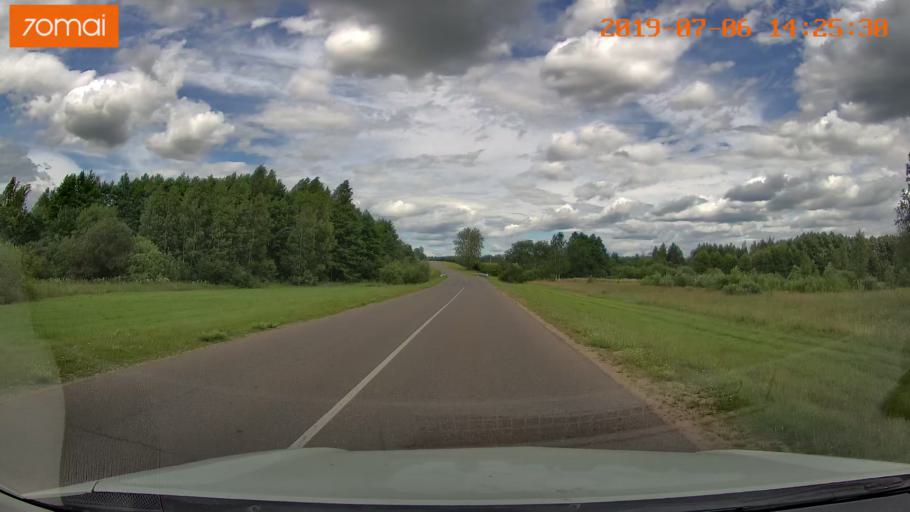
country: BY
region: Minsk
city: Ivyanyets
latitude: 53.9297
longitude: 26.7925
